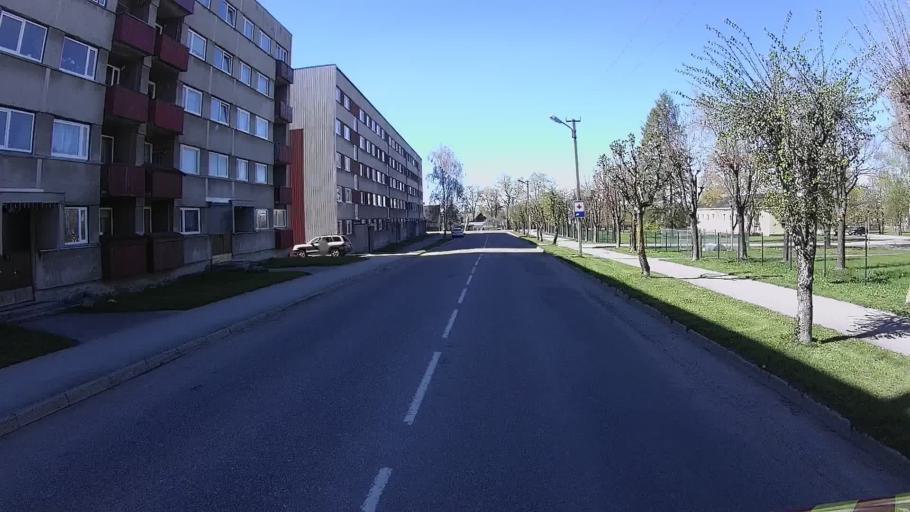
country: EE
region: Laeaene-Virumaa
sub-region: Tapa vald
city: Tapa
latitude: 59.2685
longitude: 25.9642
